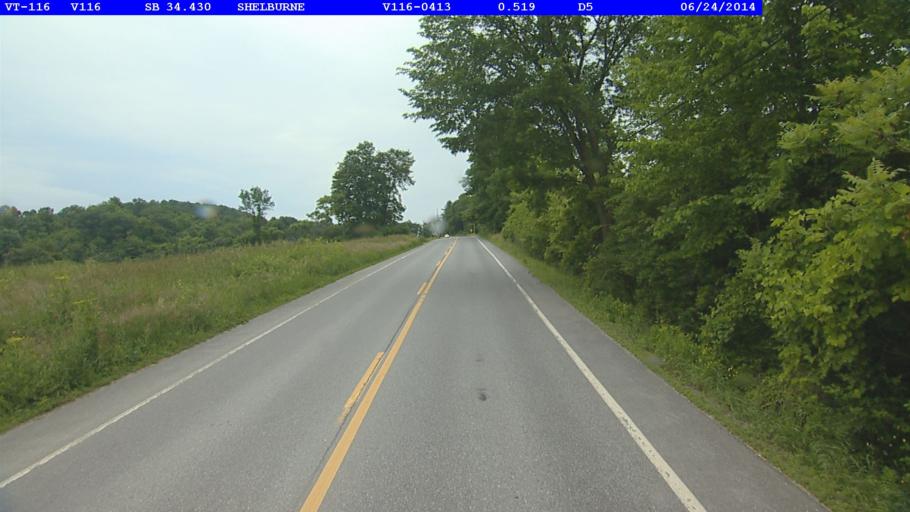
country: US
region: Vermont
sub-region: Chittenden County
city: Hinesburg
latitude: 44.3864
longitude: -73.1410
